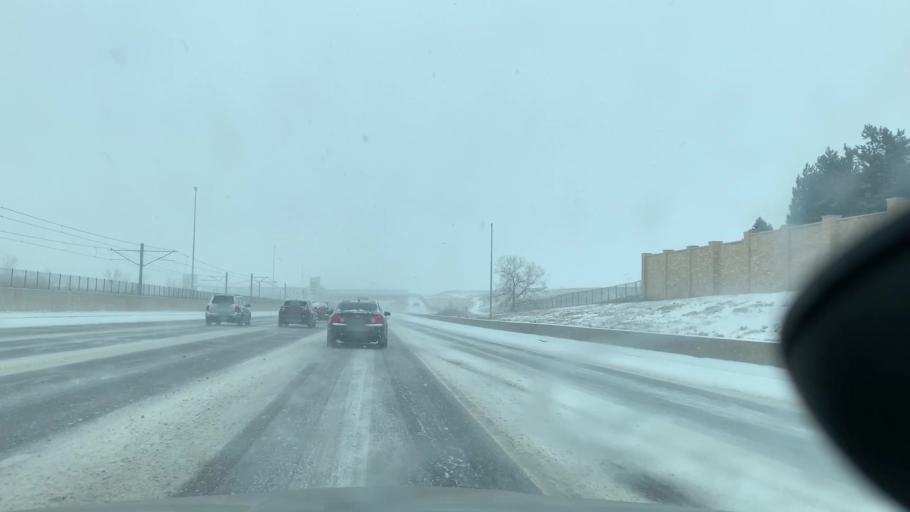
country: US
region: Colorado
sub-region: Arapahoe County
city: Castlewood
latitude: 39.6414
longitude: -104.8809
